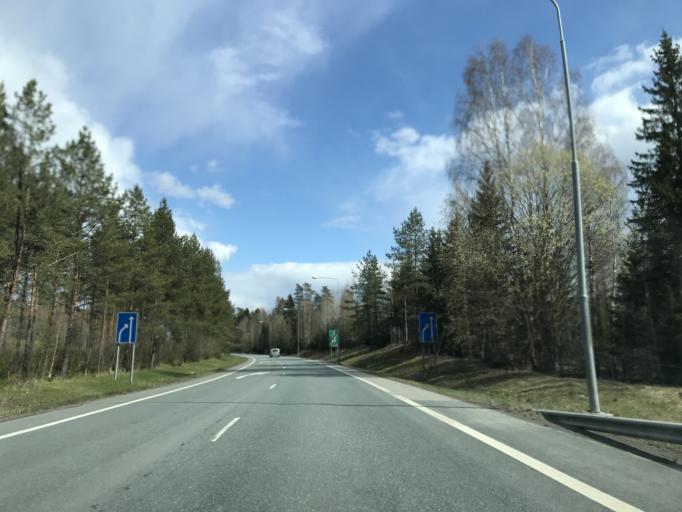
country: FI
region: Uusimaa
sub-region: Helsinki
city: Hyvinge
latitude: 60.5521
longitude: 24.8373
